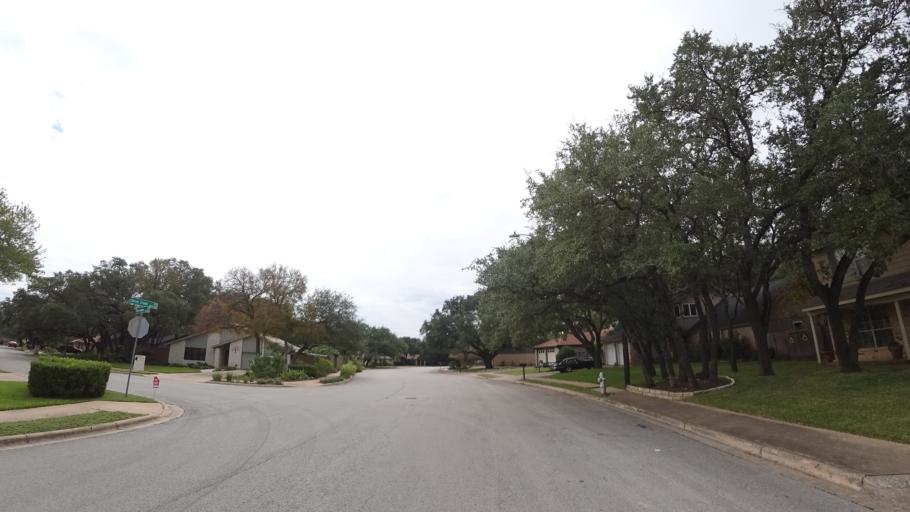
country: US
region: Texas
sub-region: Travis County
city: Wells Branch
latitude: 30.4271
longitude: -97.7144
